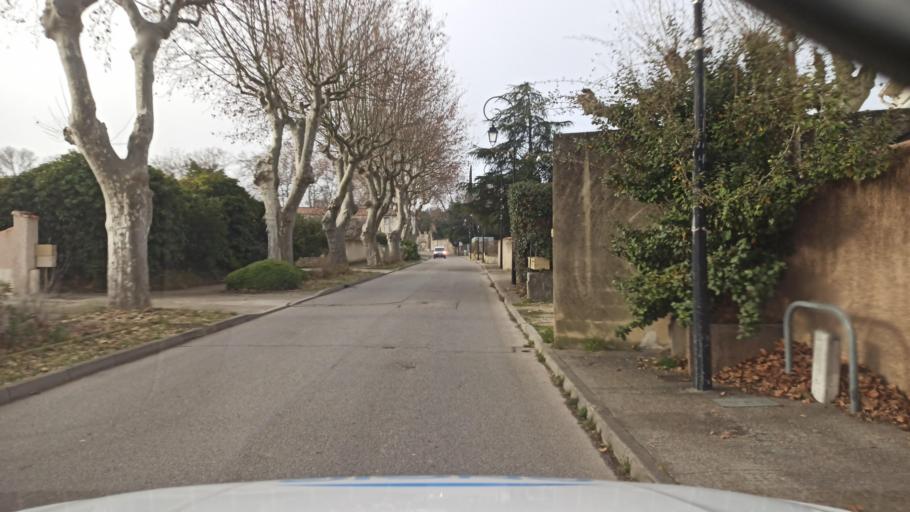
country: FR
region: Languedoc-Roussillon
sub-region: Departement du Gard
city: Aramon
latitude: 43.8930
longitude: 4.6862
